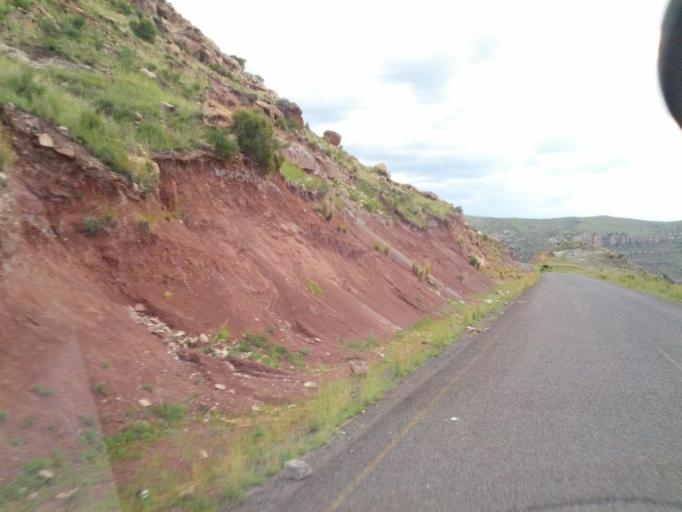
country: LS
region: Qacha's Nek
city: Qacha's Nek
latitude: -30.0629
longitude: 28.5282
